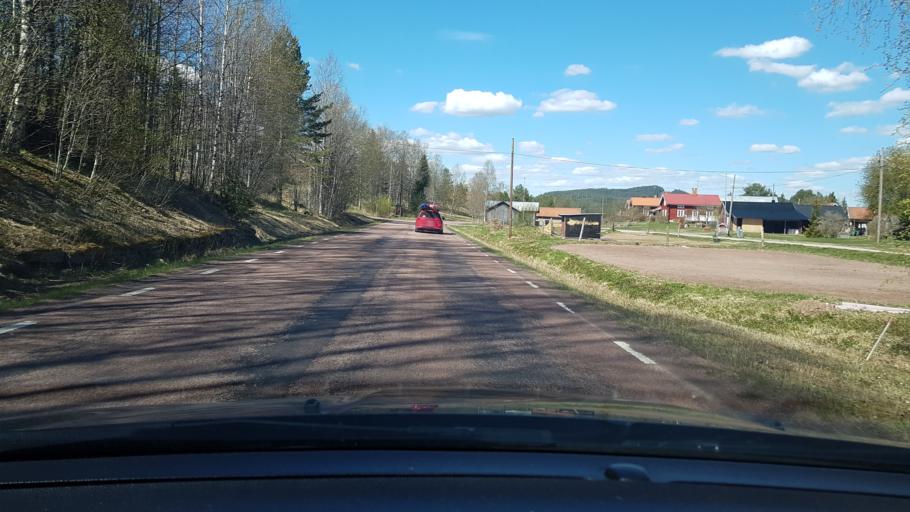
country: SE
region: Dalarna
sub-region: Alvdalens Kommun
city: AElvdalen
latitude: 61.1173
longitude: 14.1624
